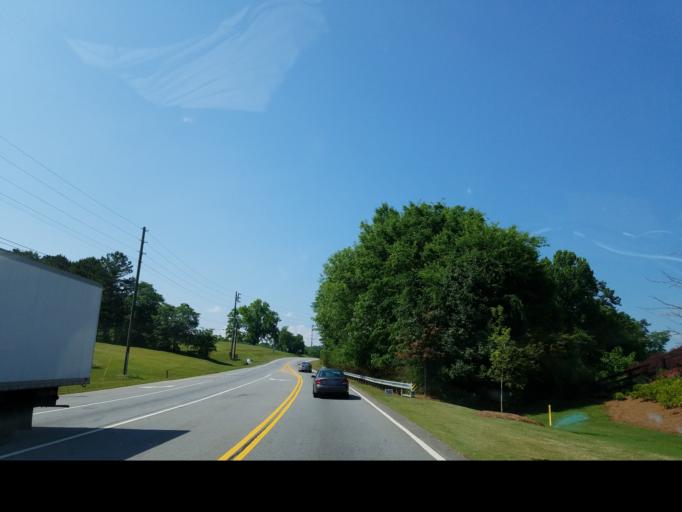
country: US
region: Georgia
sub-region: Cherokee County
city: Woodstock
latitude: 34.1065
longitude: -84.4705
